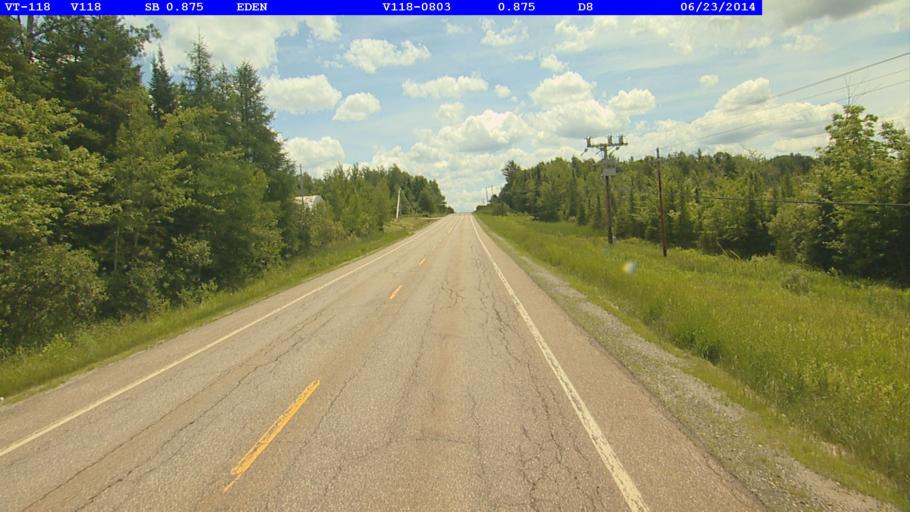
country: US
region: Vermont
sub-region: Lamoille County
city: Hyde Park
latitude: 44.7174
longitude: -72.5561
